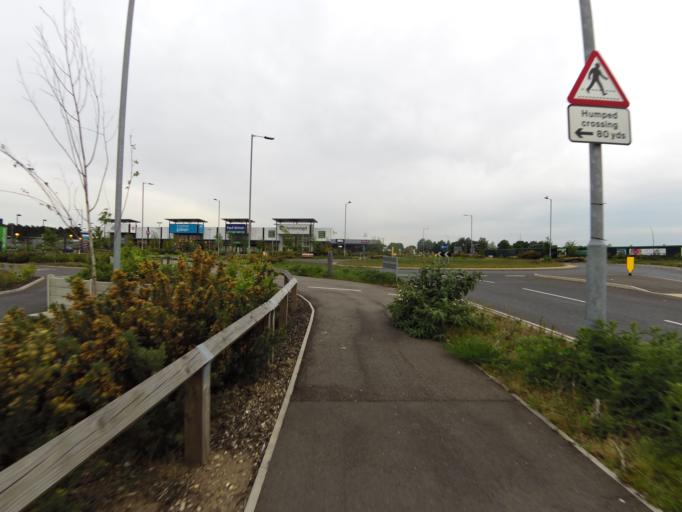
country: GB
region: England
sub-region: Suffolk
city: Kesgrave
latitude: 52.0341
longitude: 1.2028
